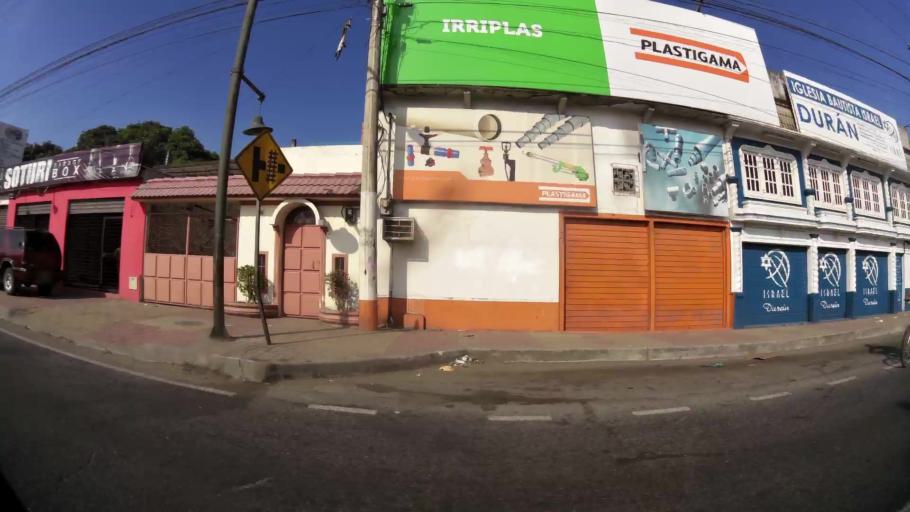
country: EC
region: Guayas
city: Eloy Alfaro
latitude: -2.1721
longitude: -79.8353
